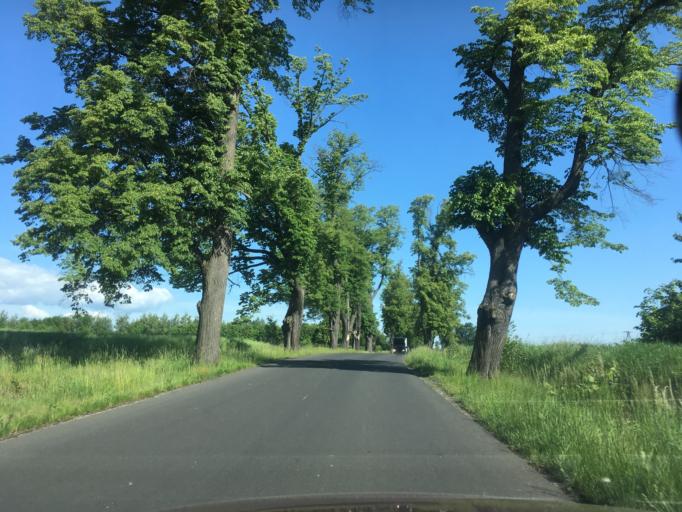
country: PL
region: Lower Silesian Voivodeship
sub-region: Powiat zgorzelecki
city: Sulikow
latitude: 51.0985
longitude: 15.0394
